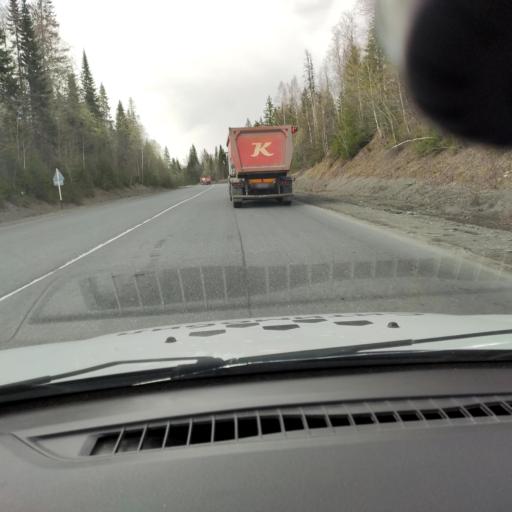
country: RU
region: Perm
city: Gremyachinsk
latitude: 58.4496
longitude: 57.8722
